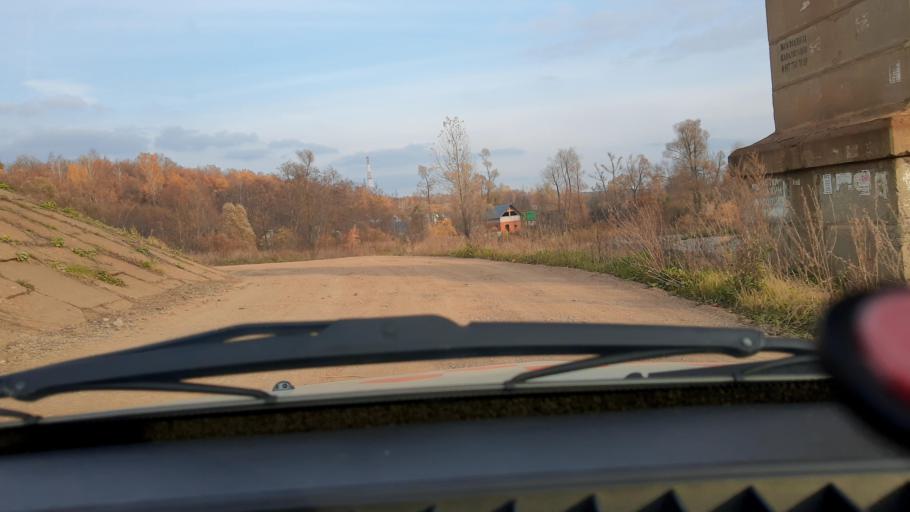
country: RU
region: Bashkortostan
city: Iglino
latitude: 54.7917
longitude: 56.3330
